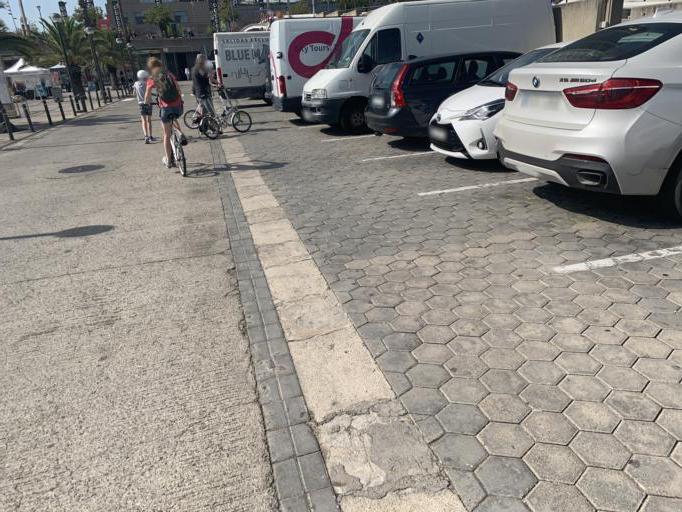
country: ES
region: Catalonia
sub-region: Provincia de Barcelona
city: Ciutat Vella
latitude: 41.3876
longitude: 2.1988
